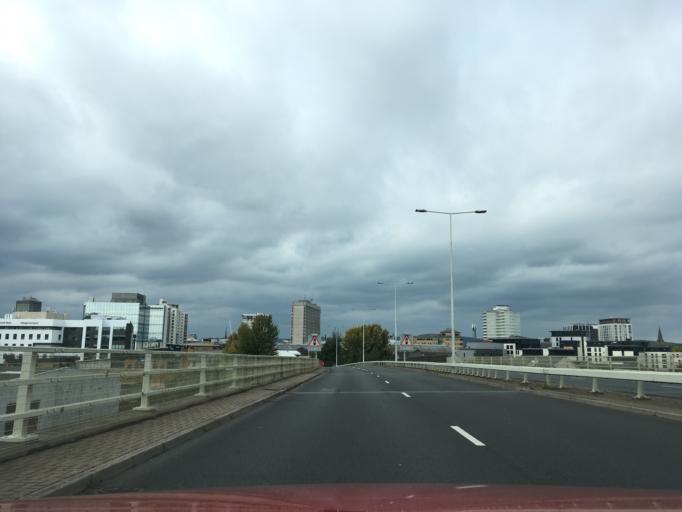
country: GB
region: Wales
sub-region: Cardiff
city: Cardiff
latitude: 51.4774
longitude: -3.1652
